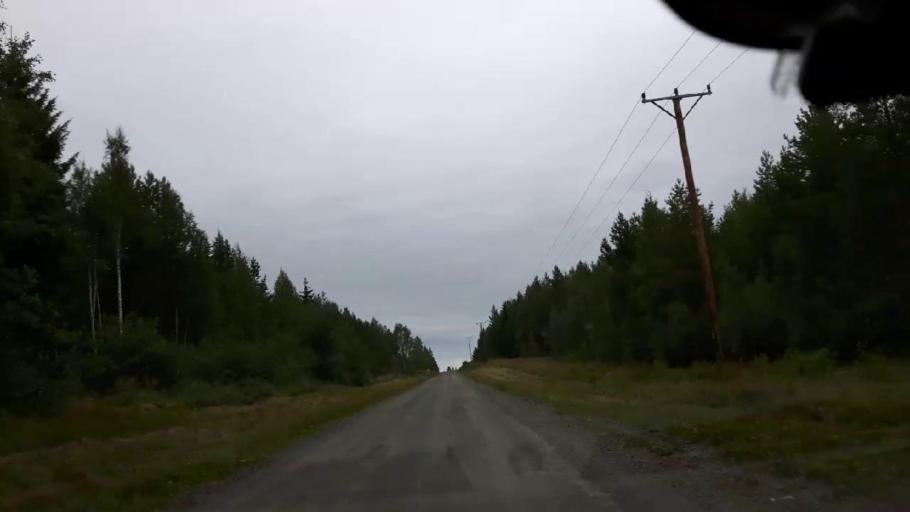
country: SE
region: Vaesternorrland
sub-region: Ange Kommun
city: Fransta
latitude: 62.8050
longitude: 16.0209
